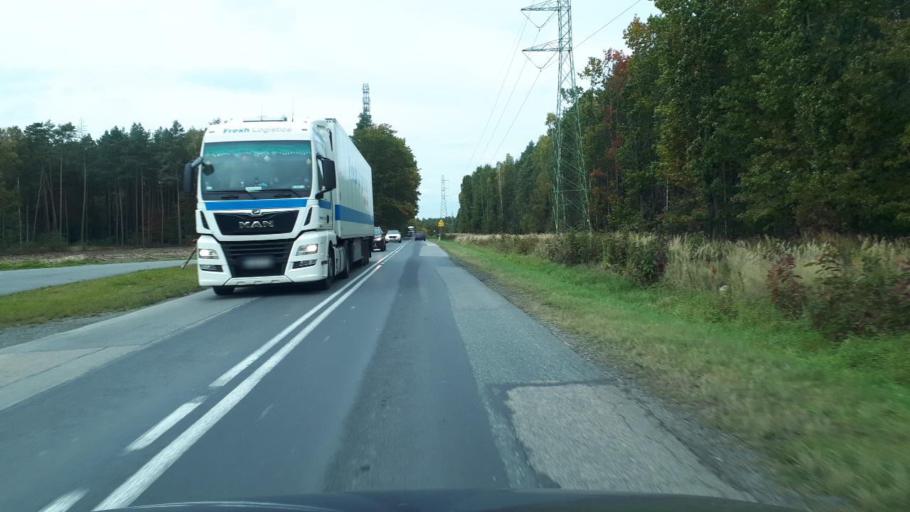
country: PL
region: Opole Voivodeship
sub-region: Powiat oleski
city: Olesno
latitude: 50.8122
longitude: 18.4109
